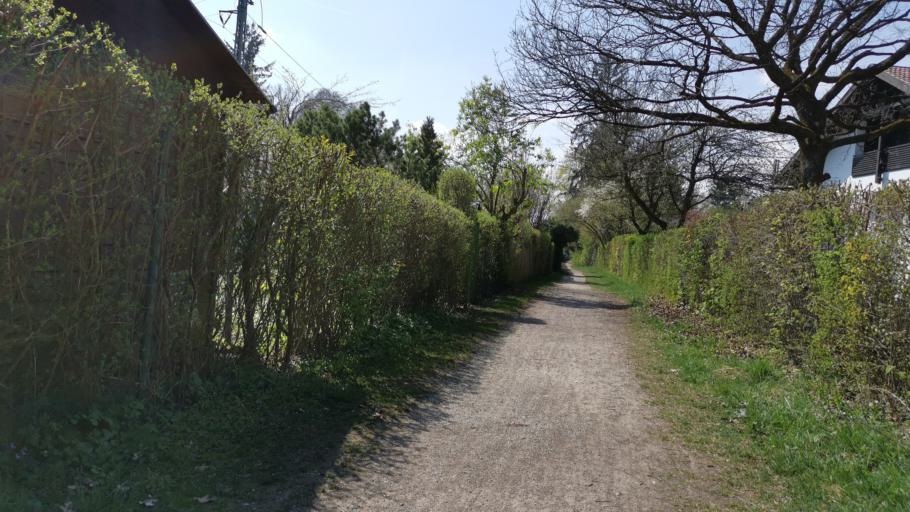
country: DE
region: Bavaria
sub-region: Upper Bavaria
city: Pullach im Isartal
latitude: 48.0857
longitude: 11.5289
